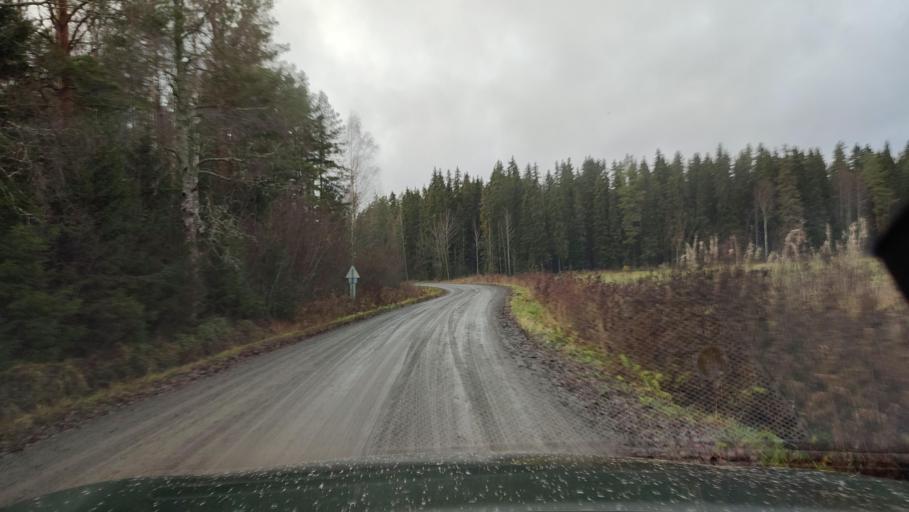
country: FI
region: Ostrobothnia
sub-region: Sydosterbotten
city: Naerpes
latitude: 62.4579
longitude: 21.4994
